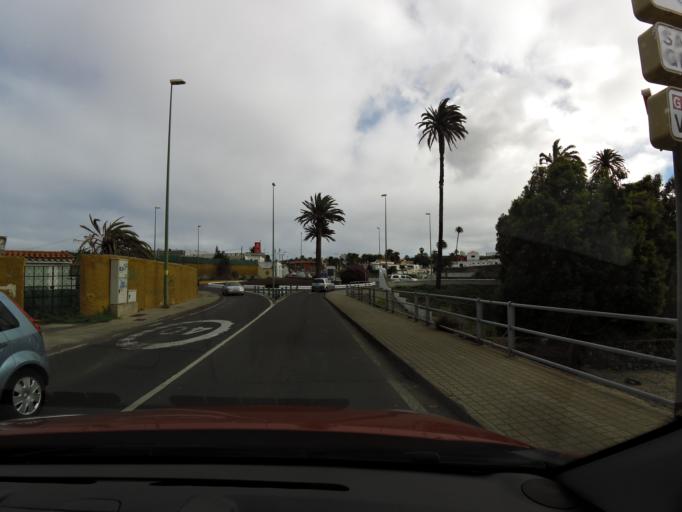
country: ES
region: Canary Islands
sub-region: Provincia de Las Palmas
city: Telde
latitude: 28.0068
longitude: -15.4163
